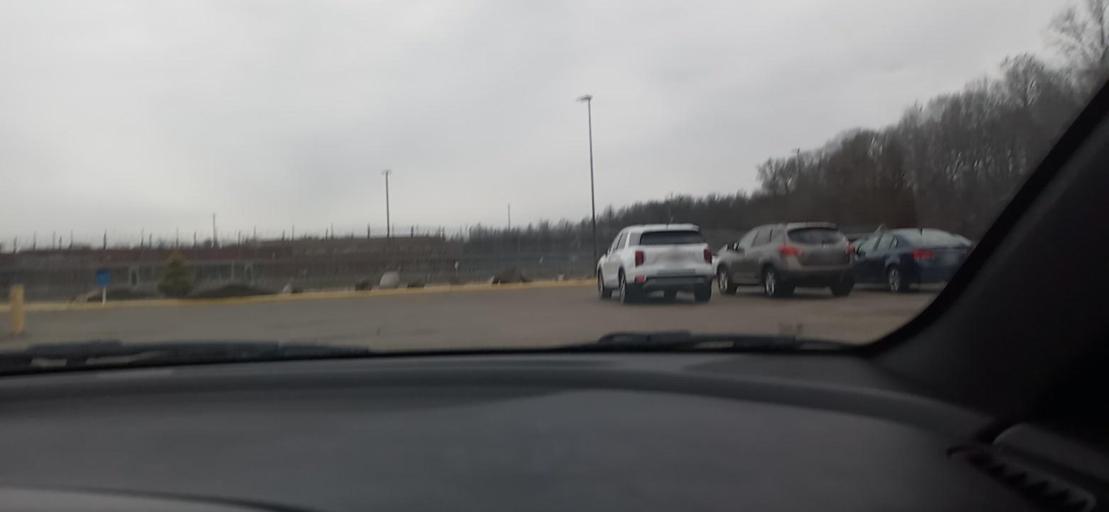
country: US
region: Ohio
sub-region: Trumbull County
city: Leavittsburg
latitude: 41.2329
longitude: -80.8887
